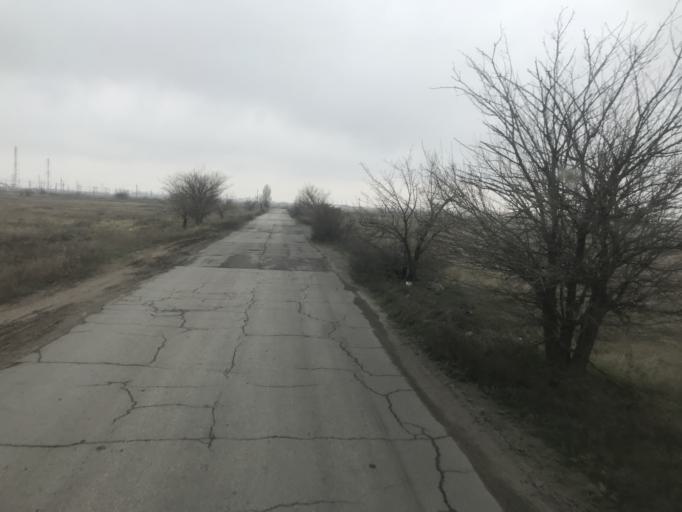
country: RU
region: Volgograd
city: Svetlyy Yar
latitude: 48.5000
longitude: 44.6465
